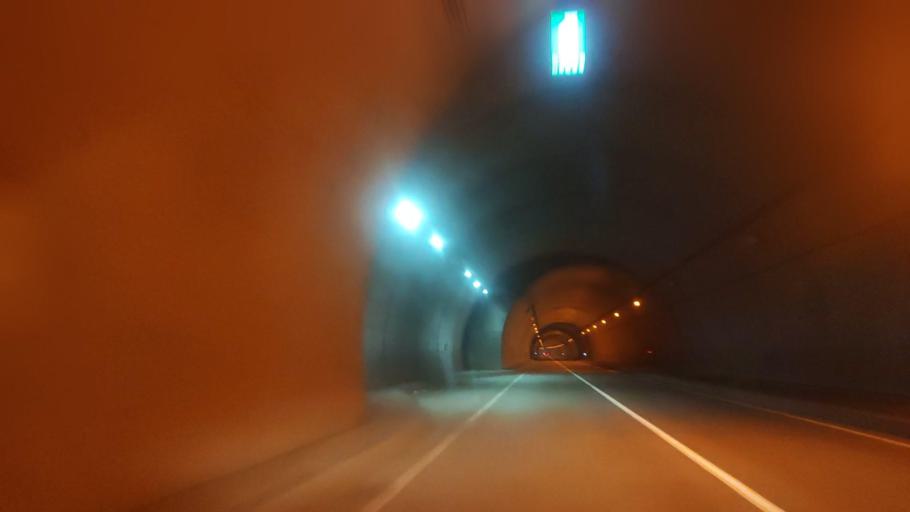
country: JP
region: Hokkaido
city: Date
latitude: 42.5660
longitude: 140.7908
